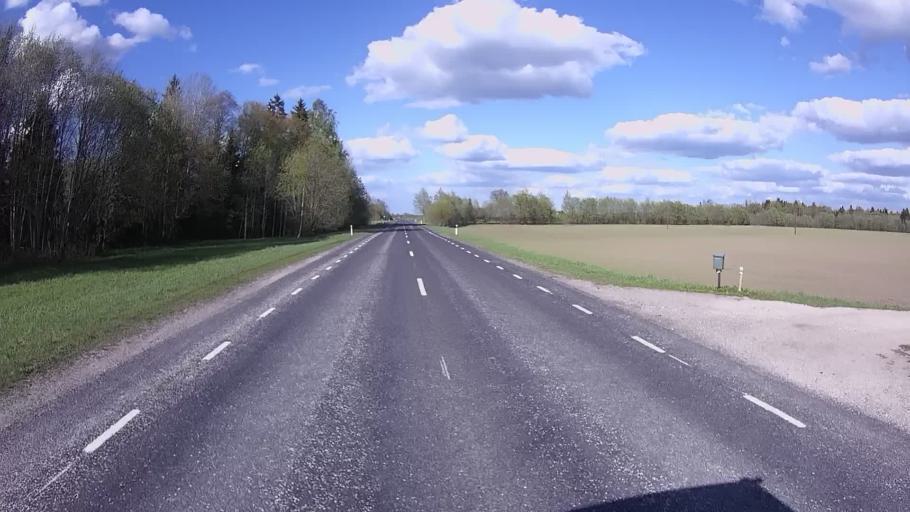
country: EE
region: Jogevamaa
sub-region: Jogeva linn
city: Jogeva
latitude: 58.7158
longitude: 26.1812
